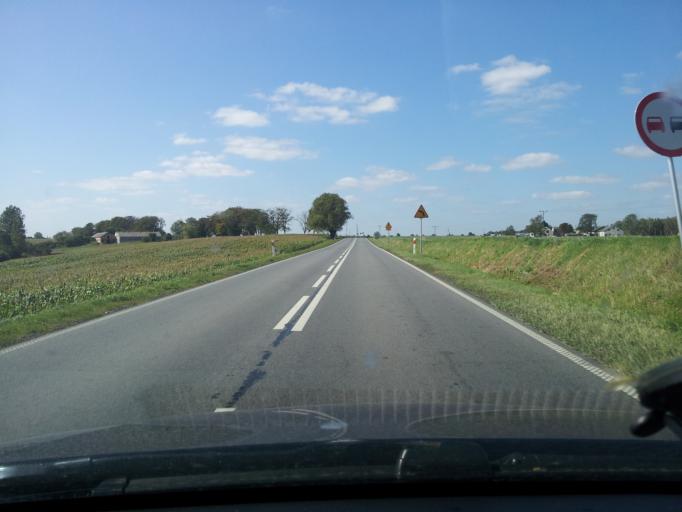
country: PL
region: Kujawsko-Pomorskie
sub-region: Powiat golubsko-dobrzynski
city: Radomin
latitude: 53.0845
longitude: 19.2170
